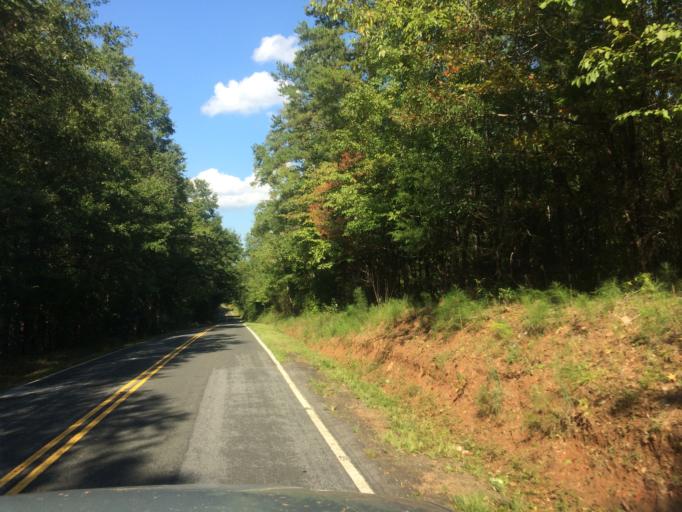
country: US
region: South Carolina
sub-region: Greenwood County
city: Ware Shoals
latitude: 34.4235
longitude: -82.2738
